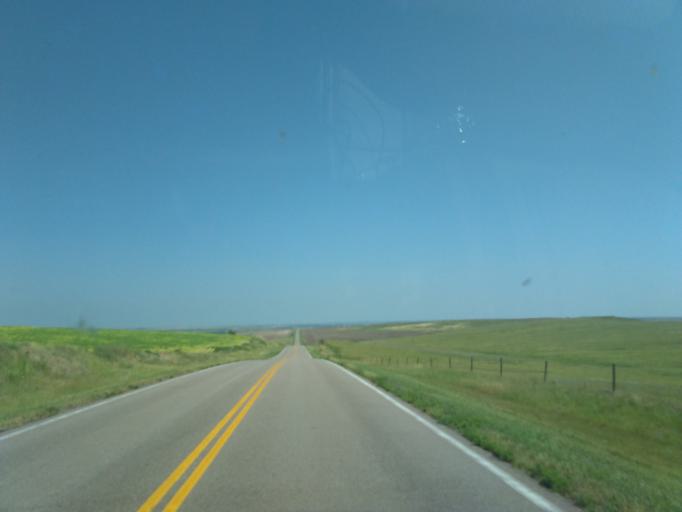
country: US
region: Nebraska
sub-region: Dundy County
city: Benkelman
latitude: 39.9551
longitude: -101.5415
